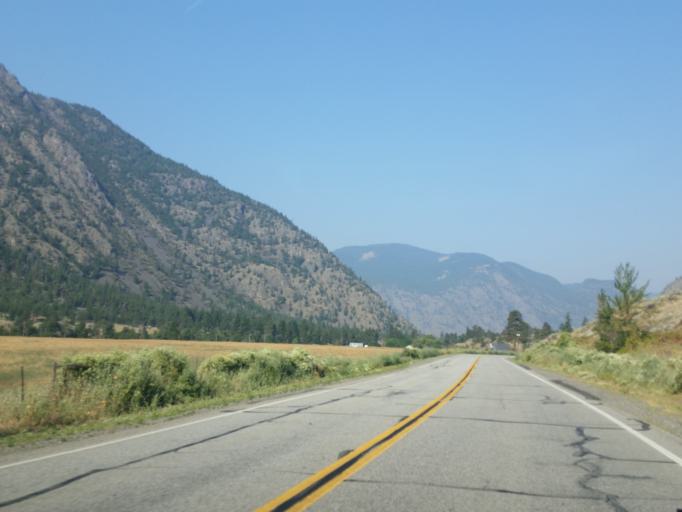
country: CA
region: British Columbia
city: Oliver
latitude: 49.2177
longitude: -119.9170
